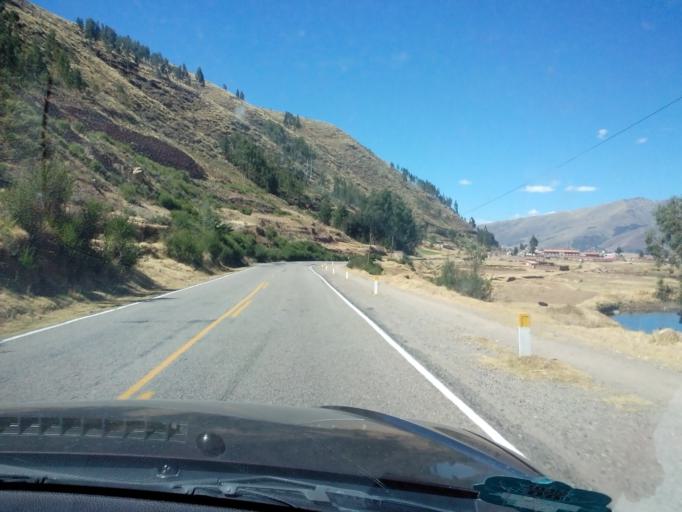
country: PE
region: Cusco
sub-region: Provincia de Canchis
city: Tinta
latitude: -14.1346
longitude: -71.4068
